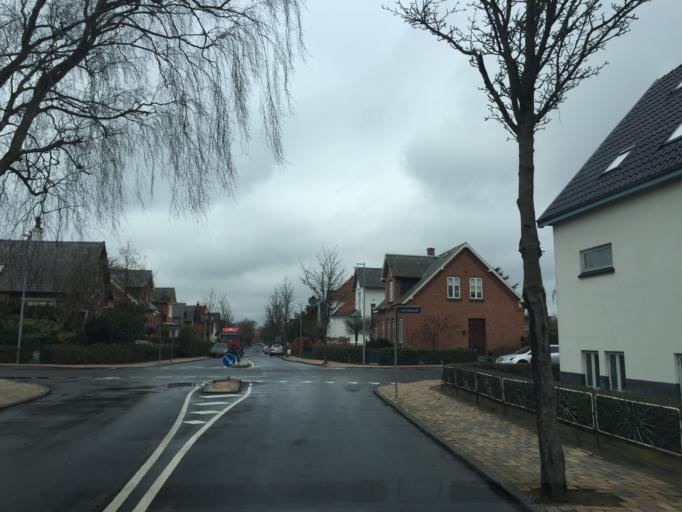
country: DK
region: South Denmark
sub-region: Odense Kommune
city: Odense
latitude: 55.3873
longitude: 10.3866
